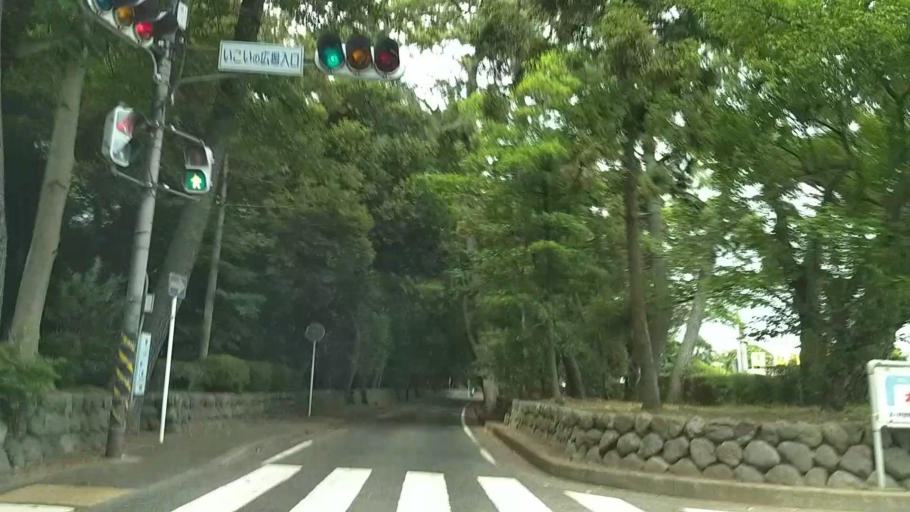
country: JP
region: Kanagawa
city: Chigasaki
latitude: 35.3742
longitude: 139.3806
